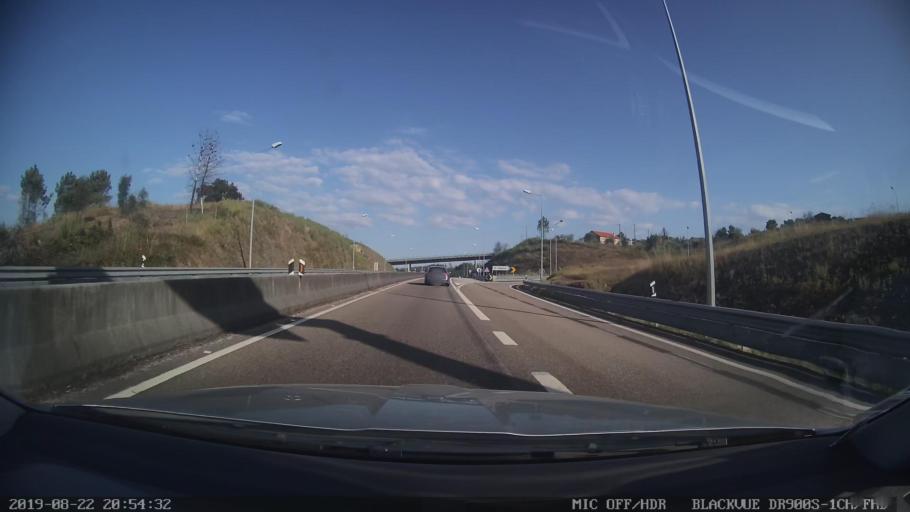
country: PT
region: Castelo Branco
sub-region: Serta
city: Serta
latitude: 39.7741
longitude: -8.0154
